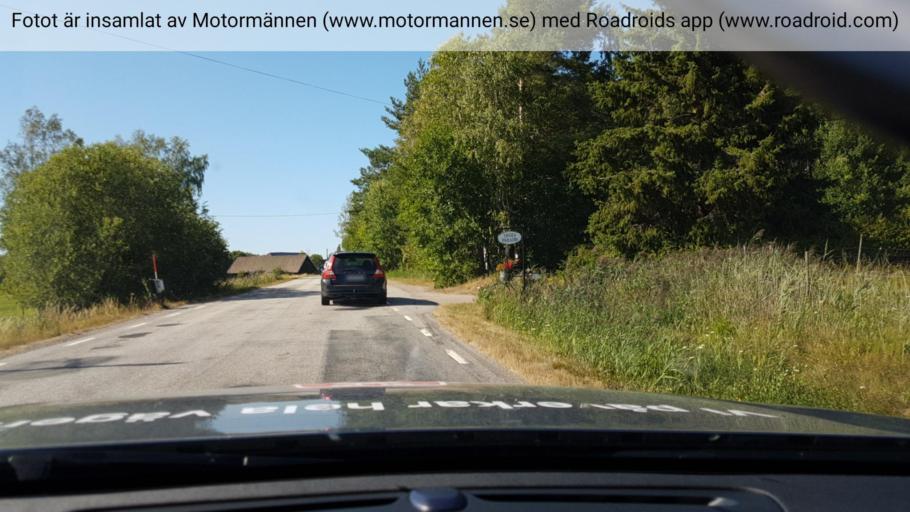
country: SE
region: Vaestra Goetaland
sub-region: Toreboda Kommun
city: Toereboda
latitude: 58.6837
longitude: 14.2058
